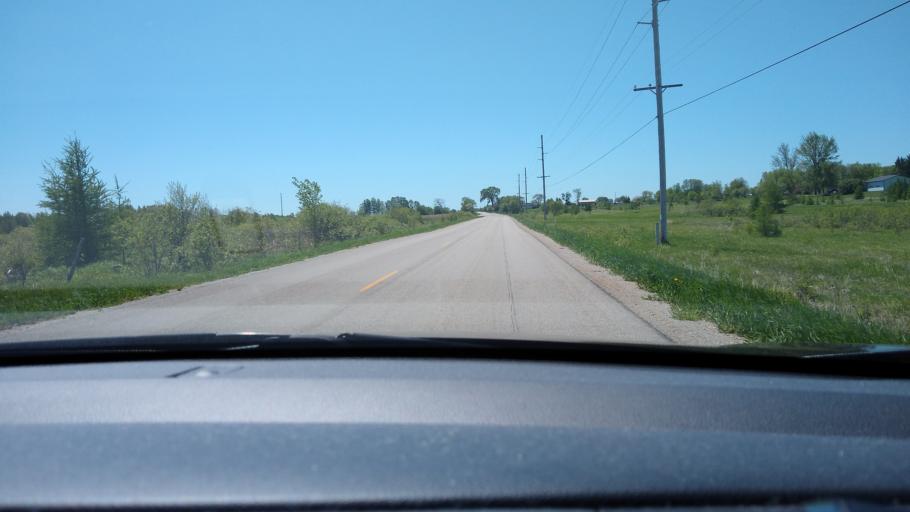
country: US
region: Michigan
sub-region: Delta County
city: Escanaba
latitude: 45.8439
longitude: -87.1842
